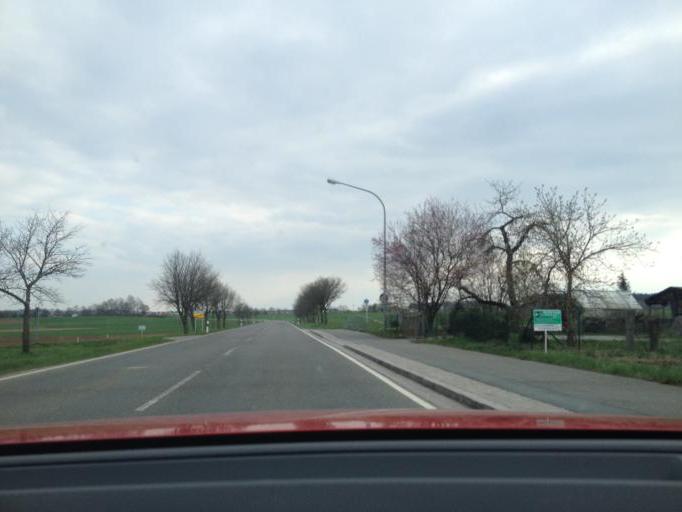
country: DE
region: Bavaria
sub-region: Upper Palatinate
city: Speinshart
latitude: 49.7736
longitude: 11.8133
